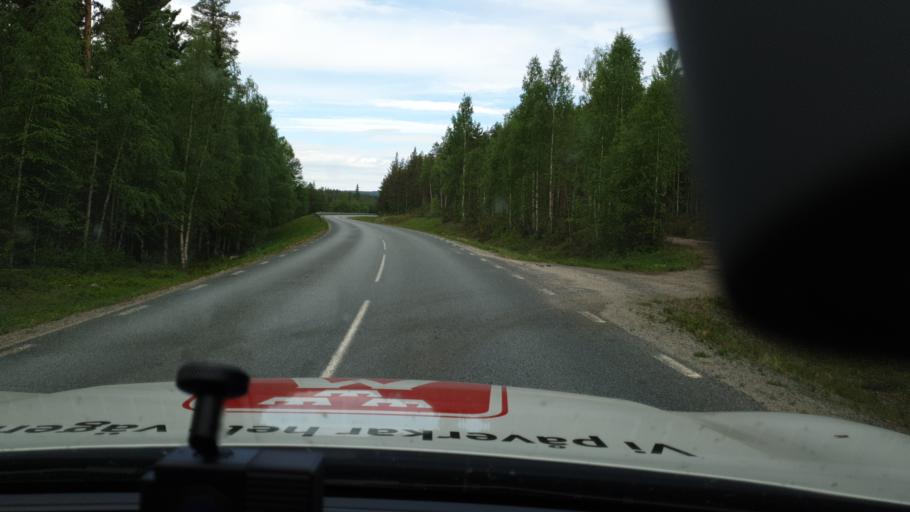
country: SE
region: Vaesterbotten
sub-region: Lycksele Kommun
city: Soderfors
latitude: 65.0785
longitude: 18.3386
